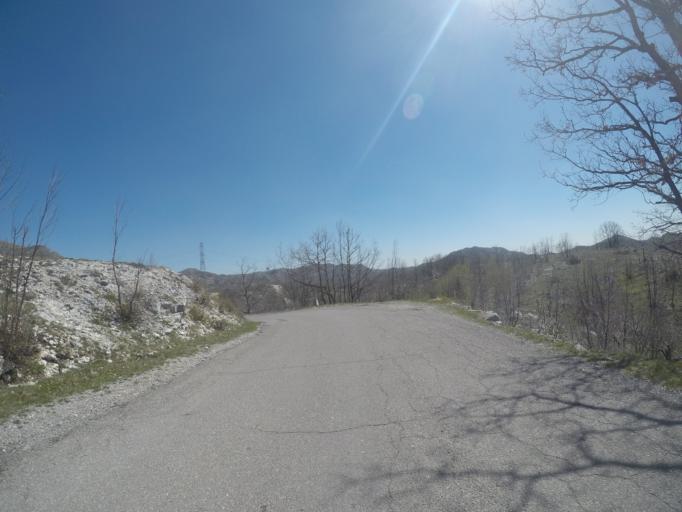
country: ME
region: Cetinje
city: Cetinje
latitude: 42.4405
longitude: 18.8740
